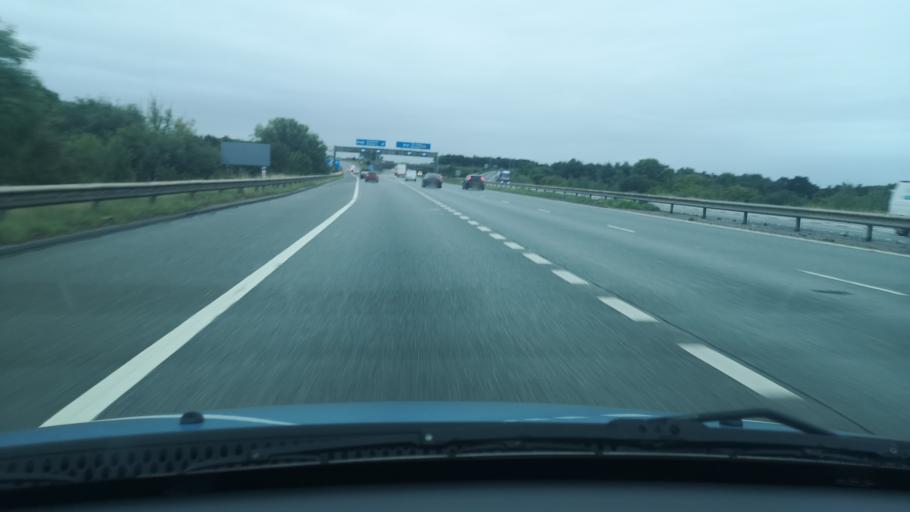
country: GB
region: England
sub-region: Doncaster
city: Hatfield
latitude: 53.5967
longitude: -0.9891
